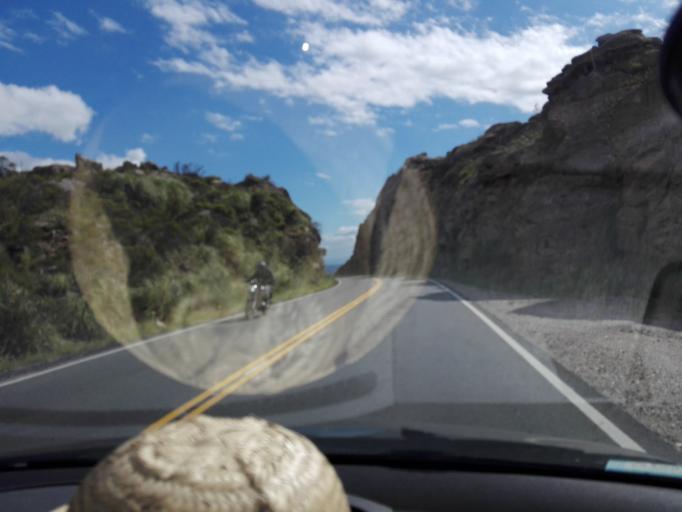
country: AR
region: Cordoba
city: Mina Clavero
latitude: -31.7609
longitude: -64.9142
